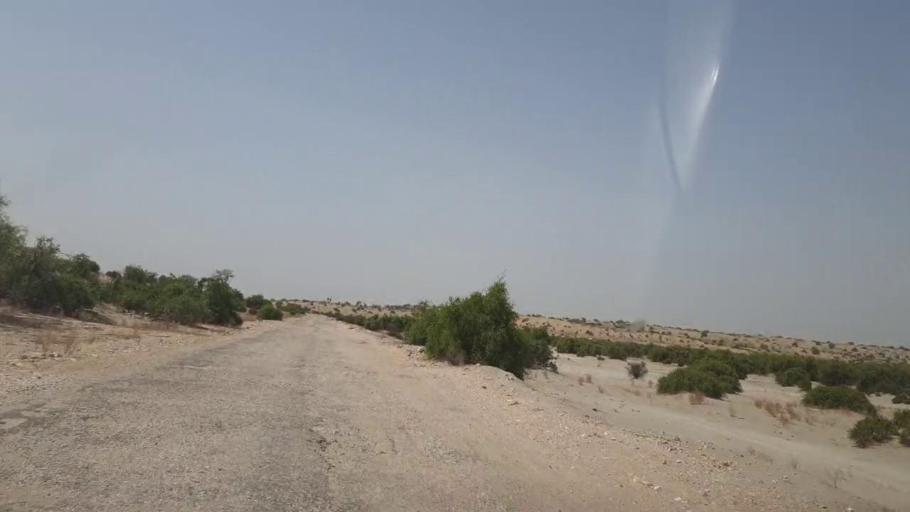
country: PK
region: Sindh
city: Khanpur
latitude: 27.3554
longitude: 69.3179
